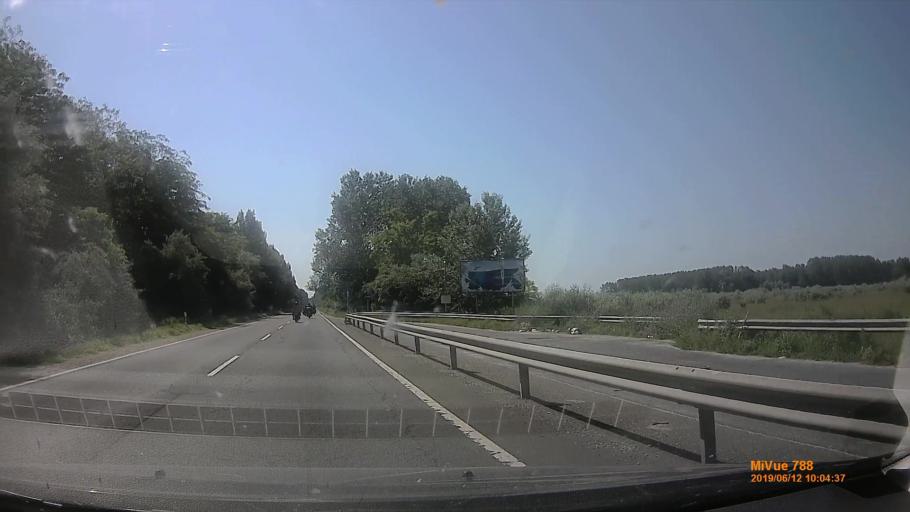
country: HU
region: Pest
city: Ocsa
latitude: 47.2891
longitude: 19.1908
